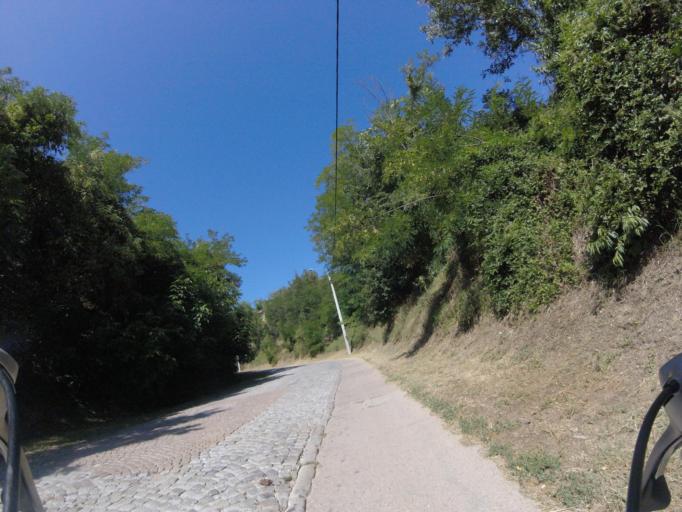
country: HR
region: Osjecko-Baranjska
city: Batina
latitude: 45.8396
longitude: 18.8402
